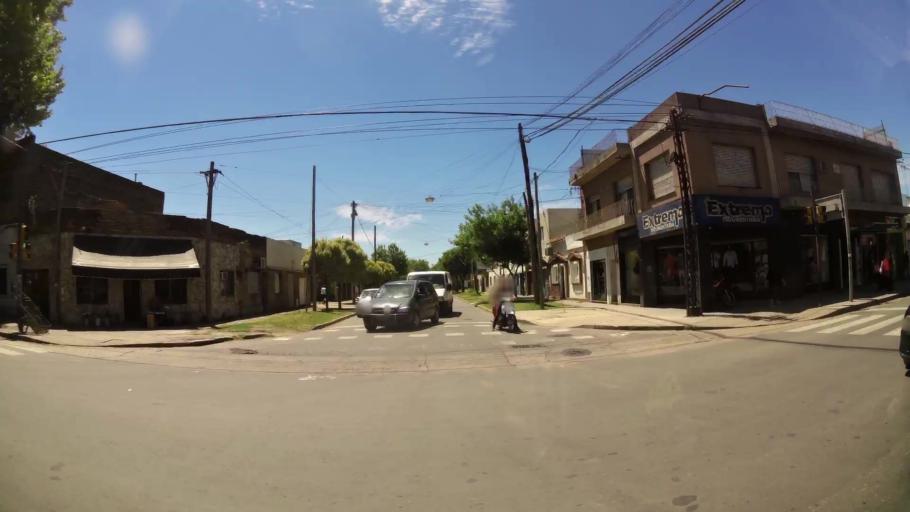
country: AR
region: Santa Fe
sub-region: Departamento de Rosario
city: Rosario
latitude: -32.9497
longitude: -60.7121
